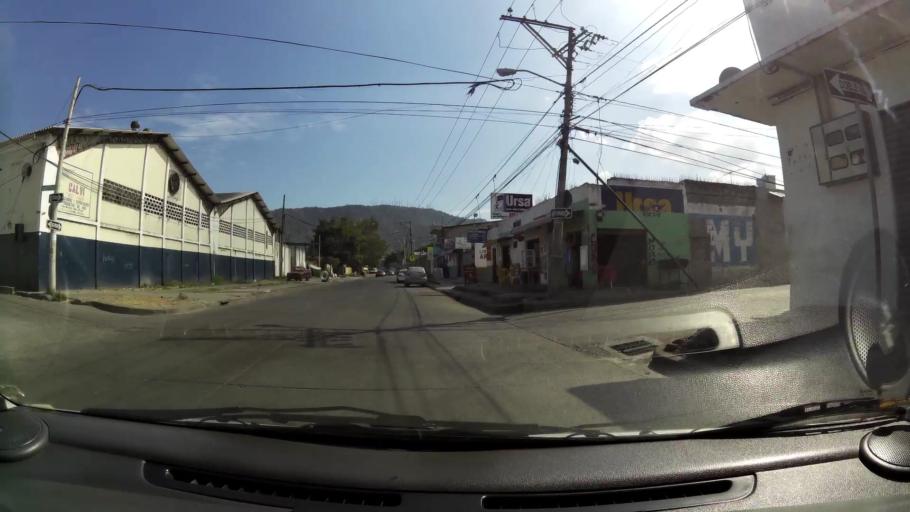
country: EC
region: Guayas
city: Guayaquil
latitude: -2.1572
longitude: -79.9357
